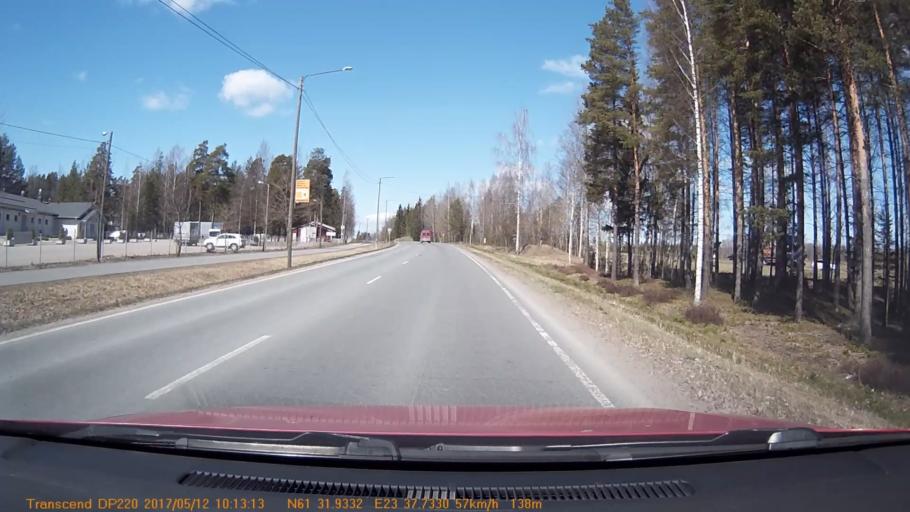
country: FI
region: Pirkanmaa
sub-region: Tampere
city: Yloejaervi
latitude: 61.5321
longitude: 23.6290
